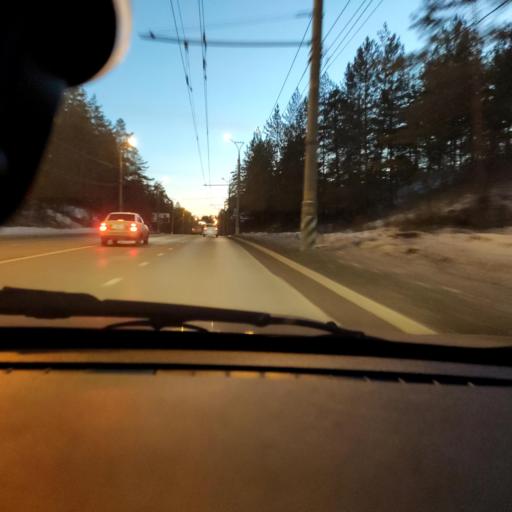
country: RU
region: Samara
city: Zhigulevsk
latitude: 53.4942
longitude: 49.4628
